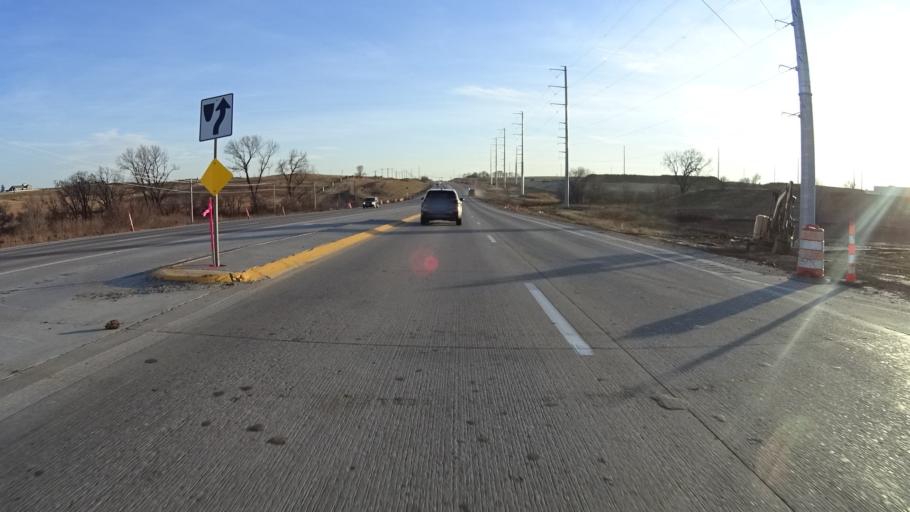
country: US
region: Nebraska
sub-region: Sarpy County
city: Chalco
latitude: 41.1401
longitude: -96.1391
